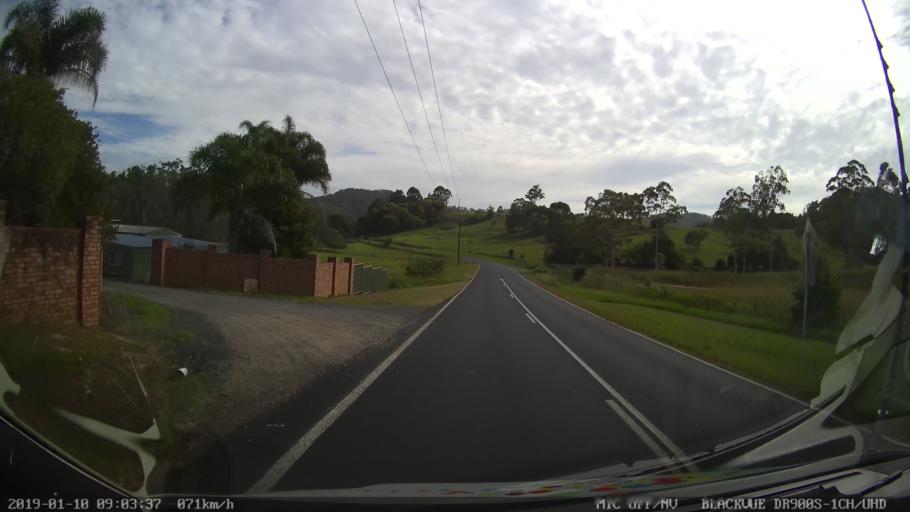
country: AU
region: New South Wales
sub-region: Coffs Harbour
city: Coffs Harbour
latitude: -30.2625
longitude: 153.0488
